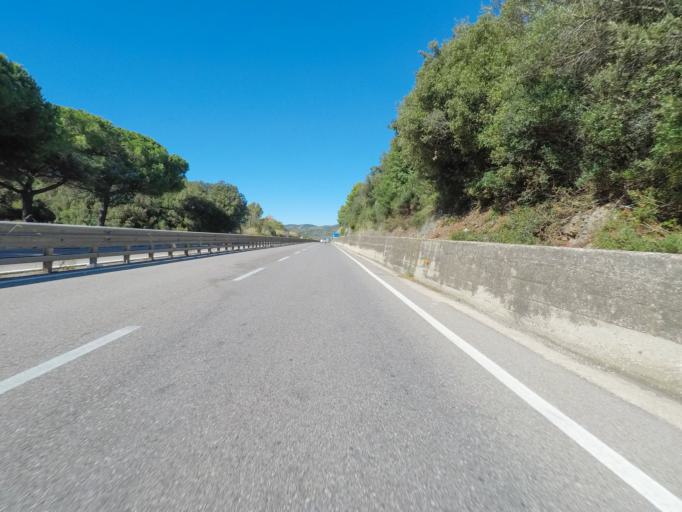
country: IT
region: Tuscany
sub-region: Provincia di Grosseto
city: Orbetello Scalo
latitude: 42.4231
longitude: 11.2887
